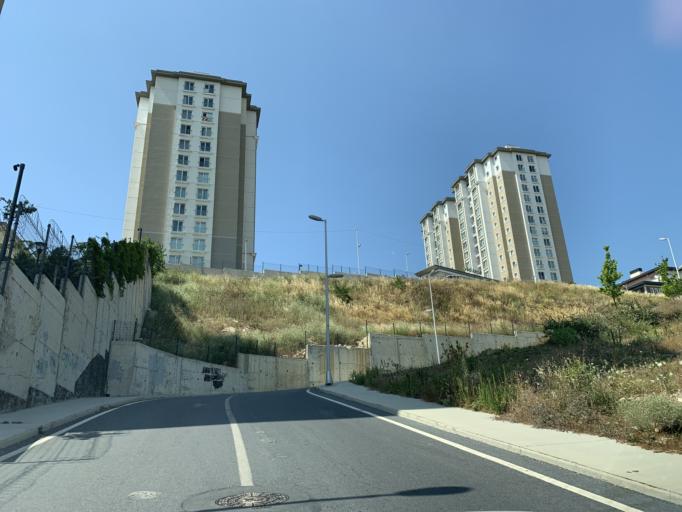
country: TR
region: Istanbul
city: Esenyurt
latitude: 41.0804
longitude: 28.6923
